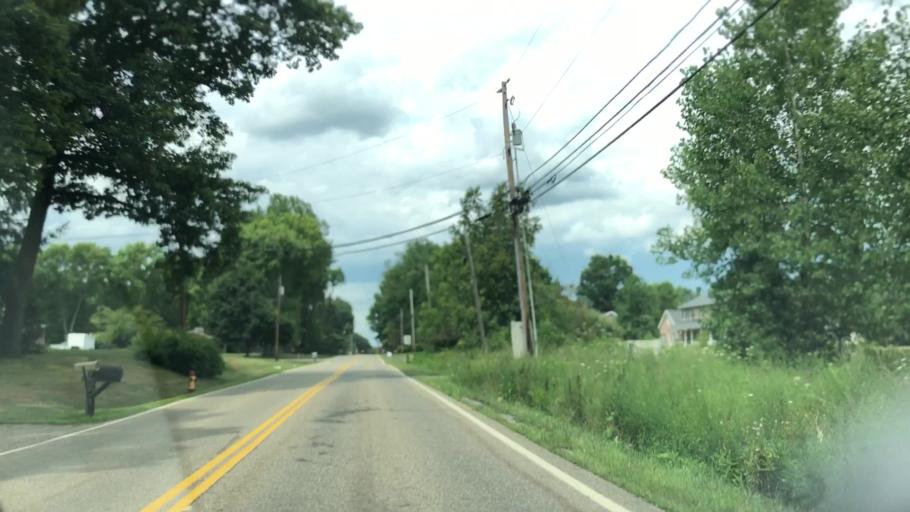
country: US
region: Ohio
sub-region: Summit County
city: Greensburg
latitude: 40.8892
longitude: -81.4596
